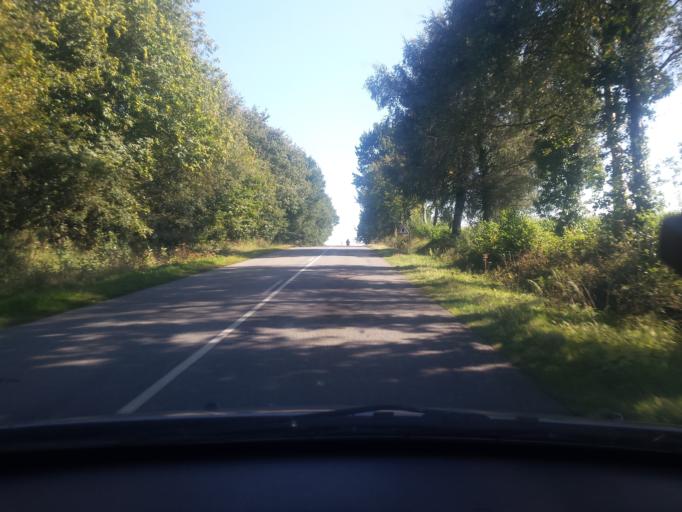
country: FR
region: Brittany
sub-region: Departement du Morbihan
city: Cleguerec
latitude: 48.1044
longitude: -3.1087
